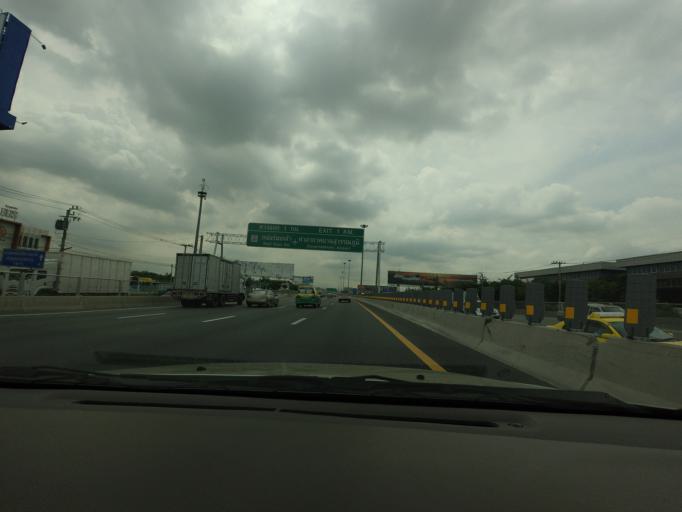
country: TH
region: Bangkok
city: Lat Krabang
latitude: 13.7295
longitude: 100.7339
